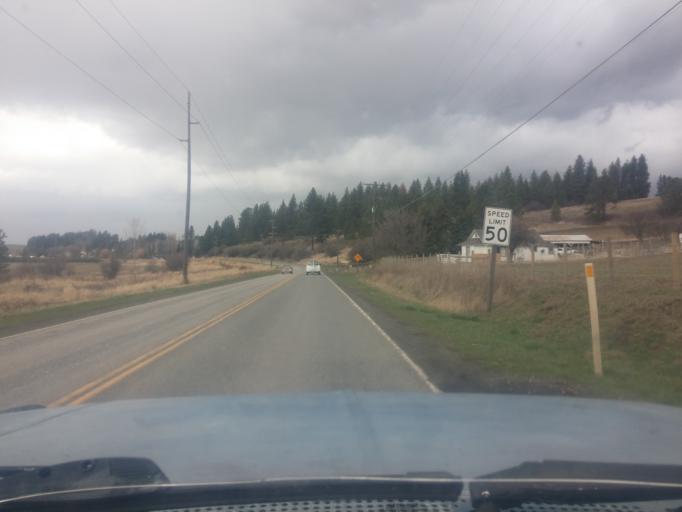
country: US
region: Idaho
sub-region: Latah County
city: Moscow
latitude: 46.9280
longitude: -116.9066
